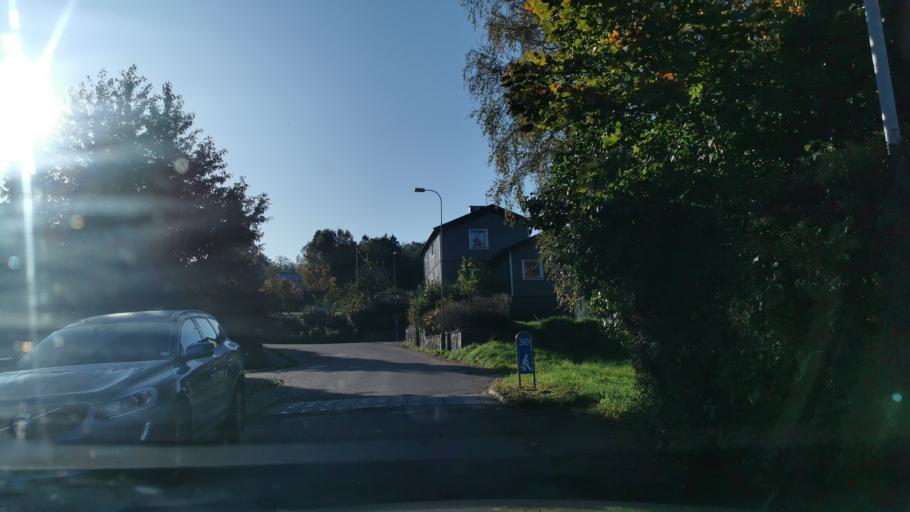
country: SE
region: Vaestra Goetaland
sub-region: Goteborg
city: Eriksbo
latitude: 57.7288
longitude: 12.0557
